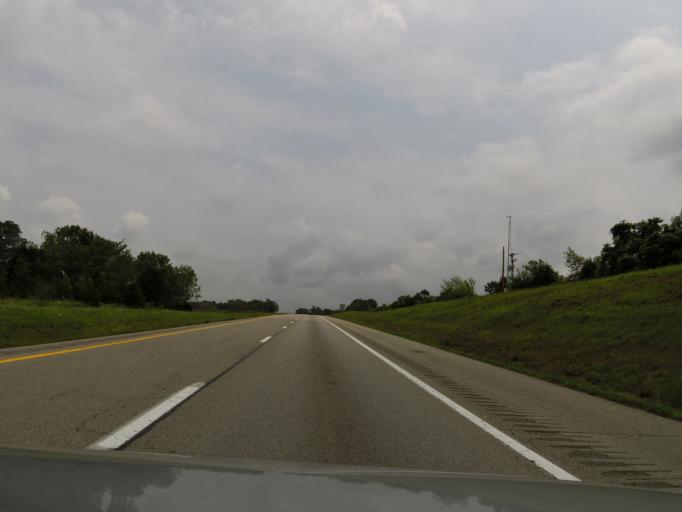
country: US
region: Kentucky
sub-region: Grayson County
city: Leitchfield
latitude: 37.4666
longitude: -86.2790
